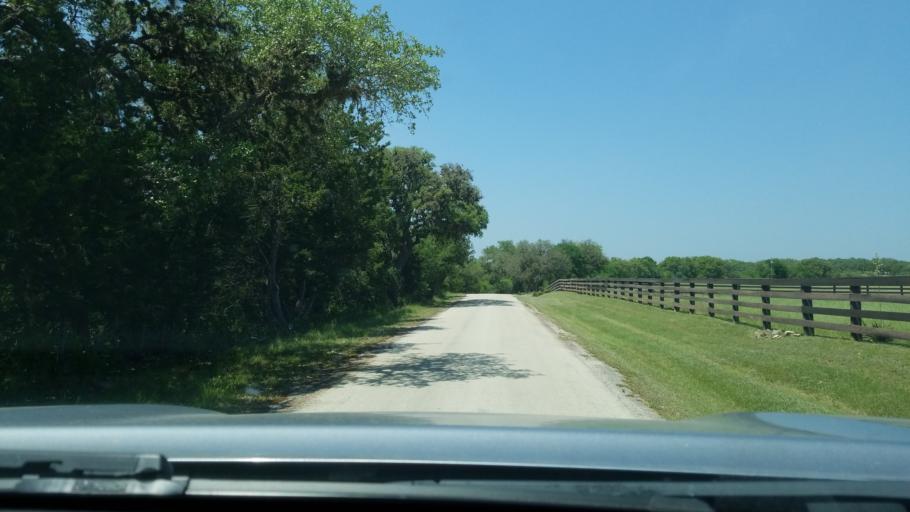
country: US
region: Texas
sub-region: Blanco County
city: Blanco
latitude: 30.0083
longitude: -98.4364
